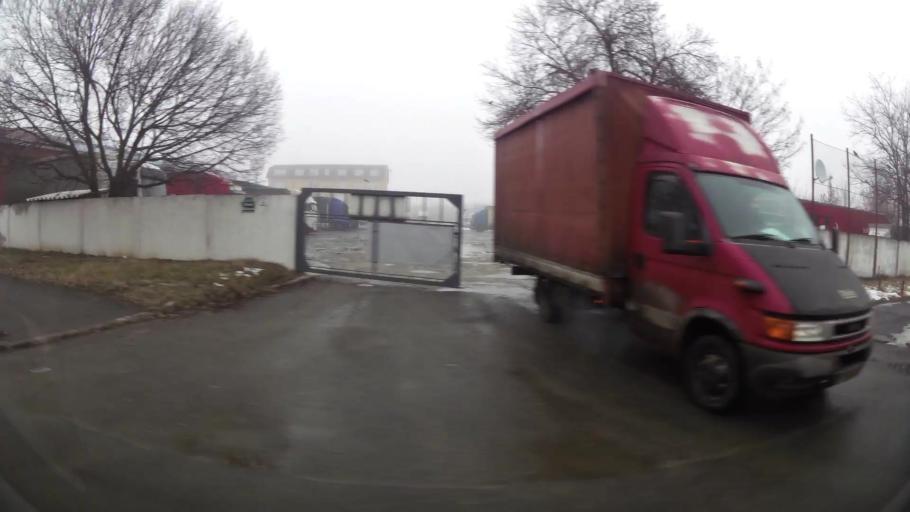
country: RO
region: Ilfov
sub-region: Comuna Chiajna
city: Rosu
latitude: 44.4719
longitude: 26.0191
